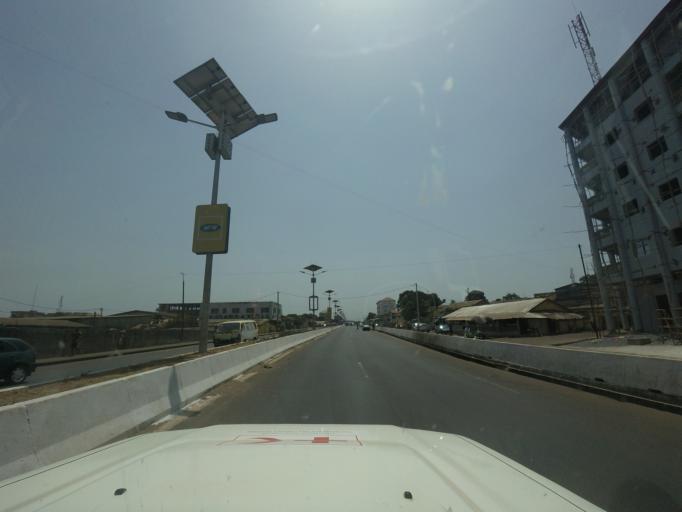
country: GN
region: Conakry
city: Conakry
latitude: 9.5583
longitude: -13.6466
